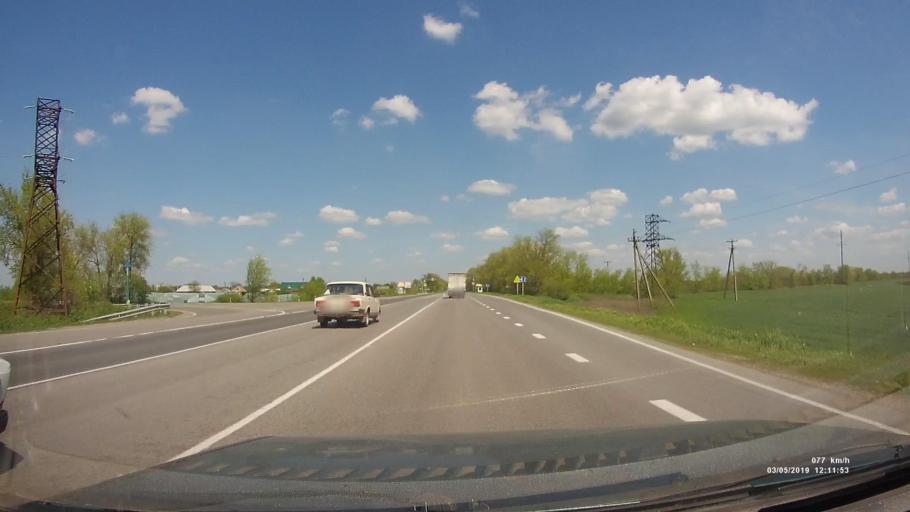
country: RU
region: Rostov
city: Bagayevskaya
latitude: 47.3154
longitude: 40.5421
